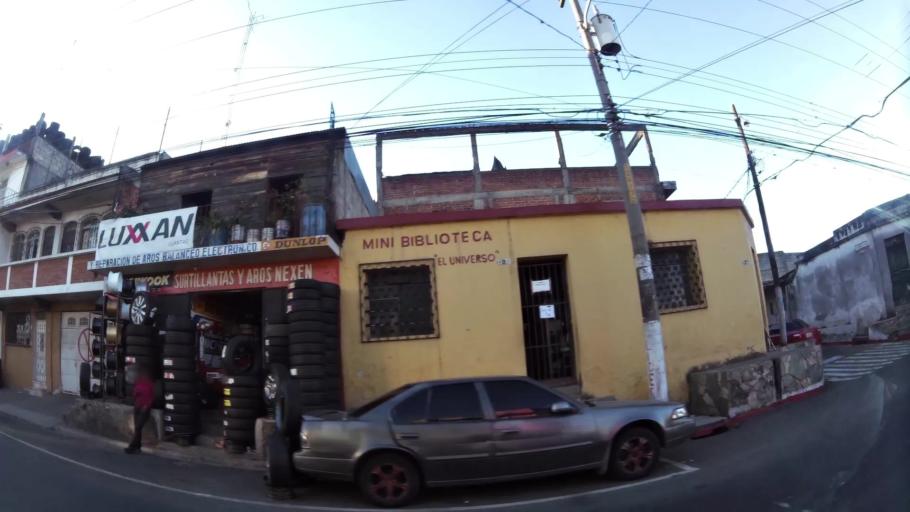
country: GT
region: Guatemala
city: Guatemala City
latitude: 14.6163
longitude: -90.5276
